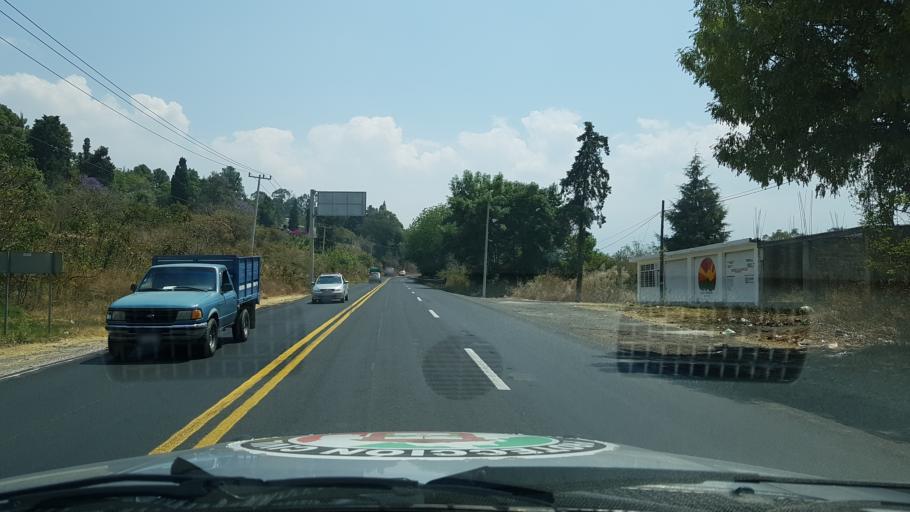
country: MX
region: Mexico
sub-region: Tepetlixpa
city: Nepantla de Sor Juana Ines de la Cruz
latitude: 18.9839
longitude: -98.8407
